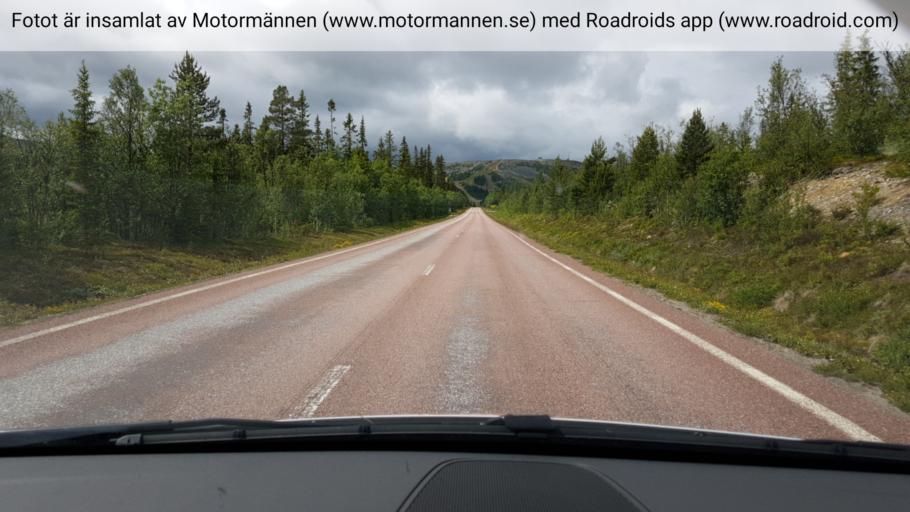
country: SE
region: Jaemtland
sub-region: Bergs Kommun
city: Hoverberg
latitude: 62.4807
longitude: 14.0066
